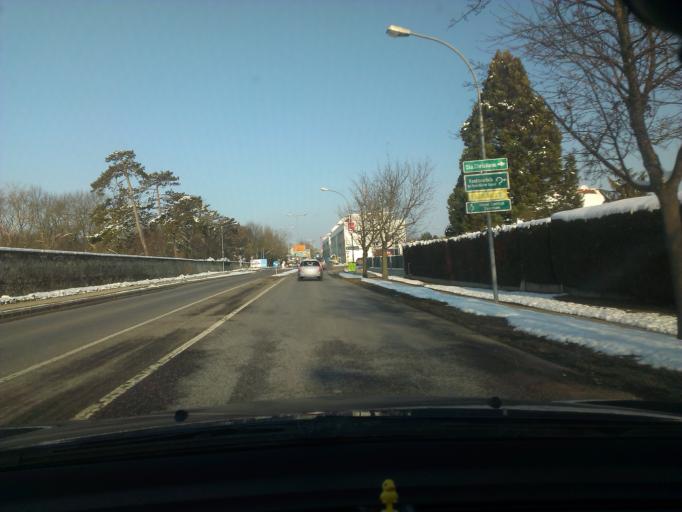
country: AT
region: Lower Austria
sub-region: Wiener Neustadt Stadt
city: Wiener Neustadt
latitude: 47.8077
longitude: 16.2602
